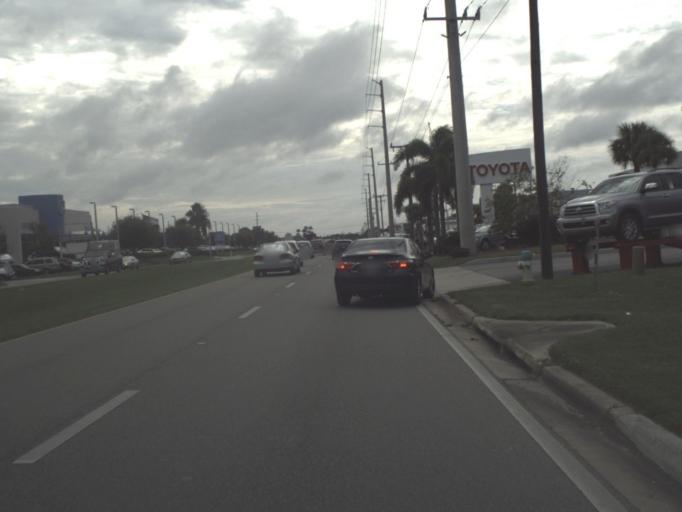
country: US
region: Florida
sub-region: Sarasota County
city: Venice
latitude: 27.0900
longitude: -82.4319
